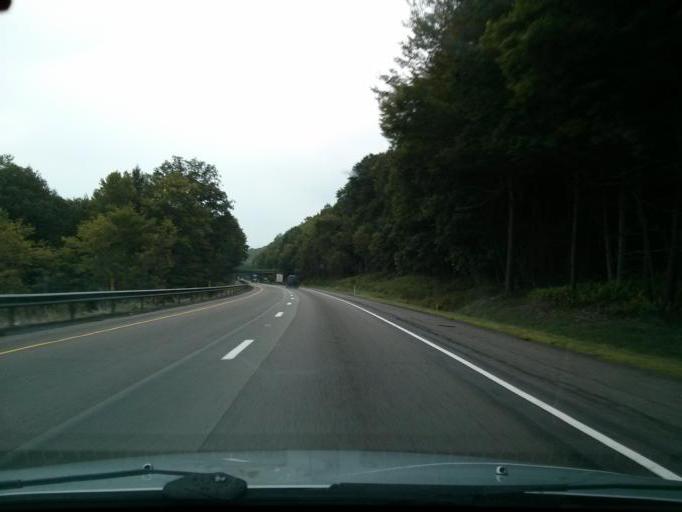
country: US
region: Pennsylvania
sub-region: Jefferson County
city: Brookville
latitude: 41.1466
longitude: -78.9949
